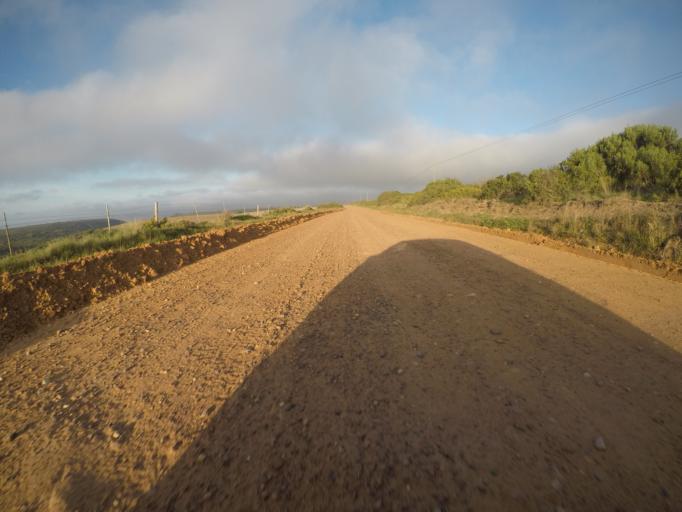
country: ZA
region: Western Cape
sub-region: Eden District Municipality
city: Mossel Bay
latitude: -34.1431
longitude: 22.0255
